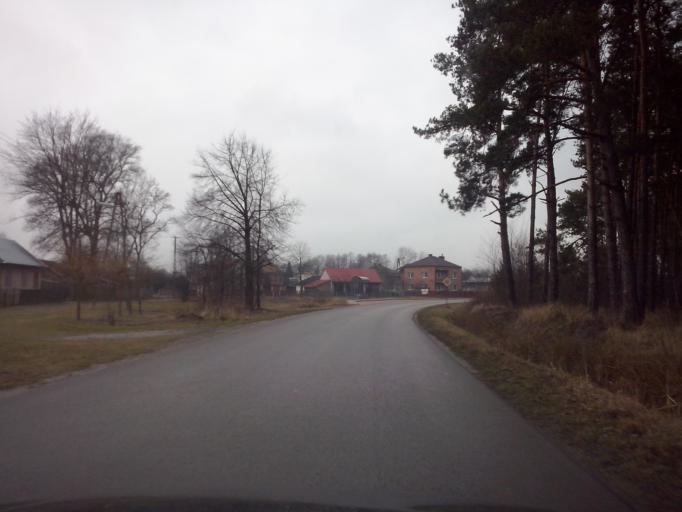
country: PL
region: Subcarpathian Voivodeship
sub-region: Powiat nizanski
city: Bieliny
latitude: 50.4459
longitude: 22.2951
